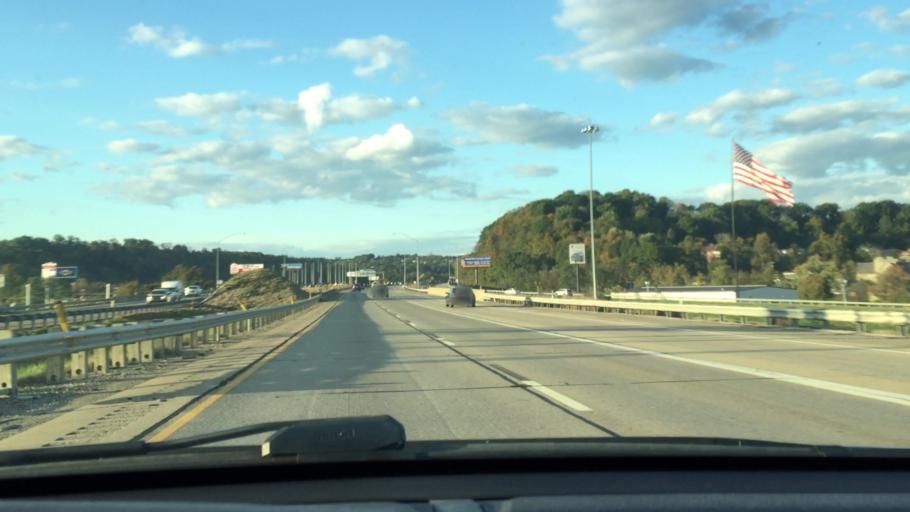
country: US
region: Pennsylvania
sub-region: Allegheny County
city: Bridgeville
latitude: 40.3550
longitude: -80.1180
